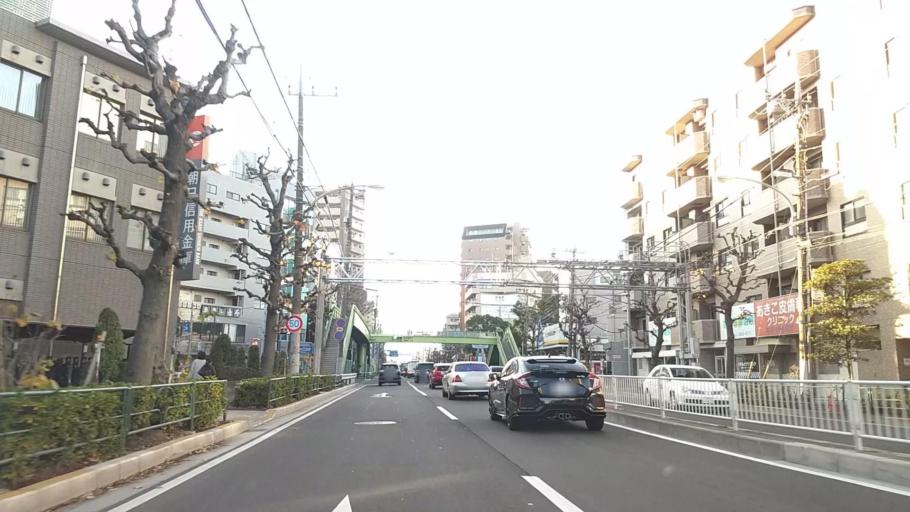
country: JP
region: Tokyo
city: Urayasu
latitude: 35.6697
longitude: 139.8598
